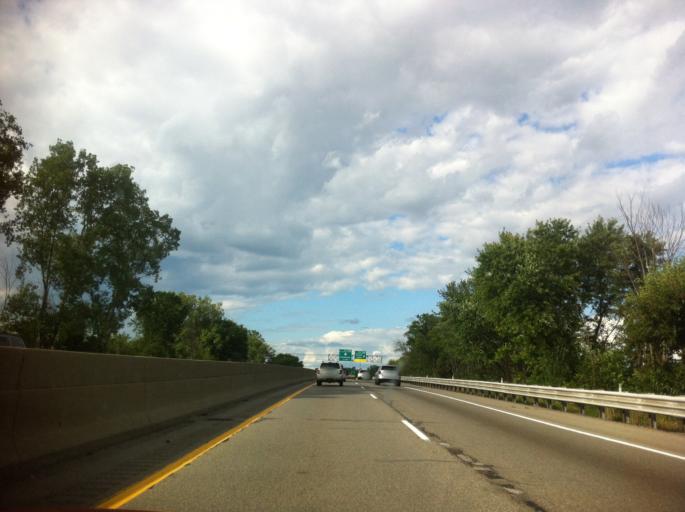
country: US
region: Michigan
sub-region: Livingston County
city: Whitmore Lake
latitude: 42.4375
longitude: -83.7573
